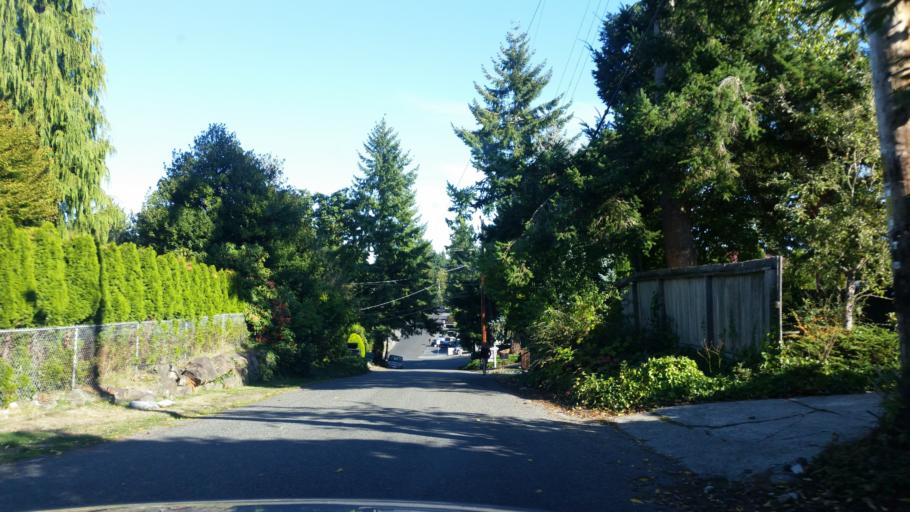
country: US
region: Washington
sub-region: King County
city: Shoreline
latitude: 47.7287
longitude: -122.3569
